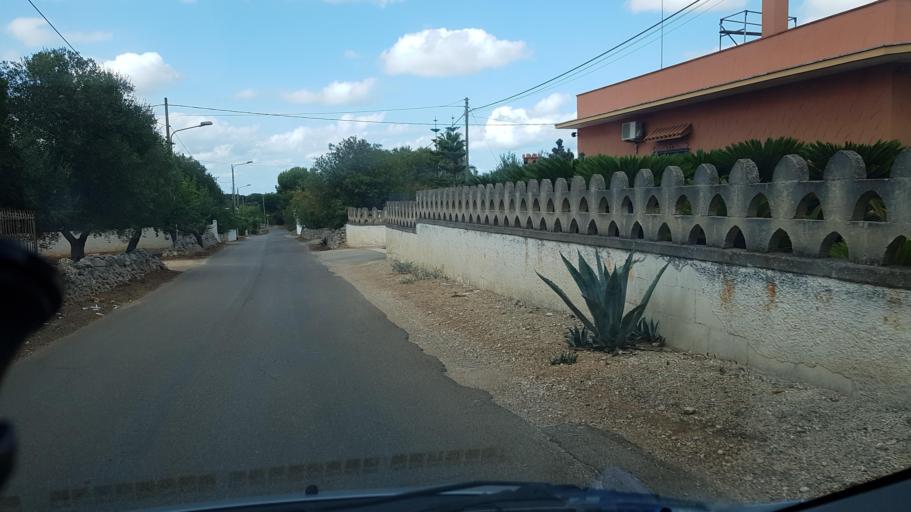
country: IT
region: Apulia
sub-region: Provincia di Brindisi
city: San Vito dei Normanni
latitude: 40.6649
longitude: 17.7161
